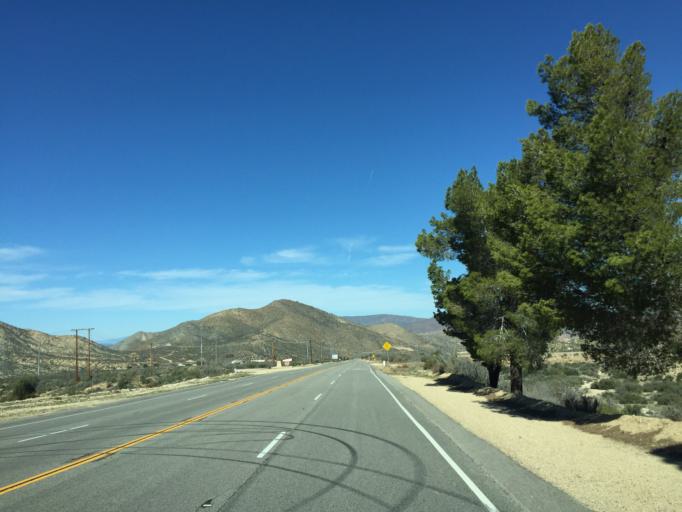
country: US
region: California
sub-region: Los Angeles County
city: Vincent
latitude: 34.4431
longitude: -118.0981
